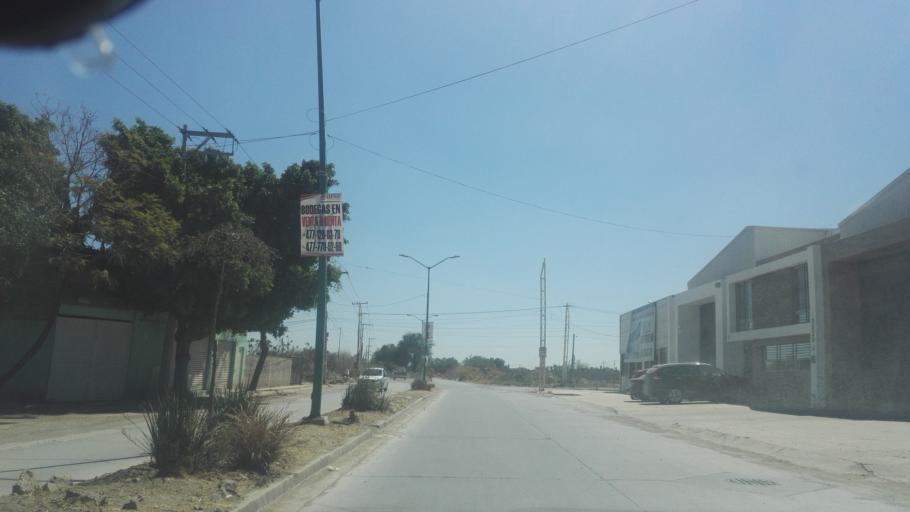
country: MX
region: Guanajuato
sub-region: Leon
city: Fraccionamiento Paraiso Real
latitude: 21.0886
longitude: -101.5934
